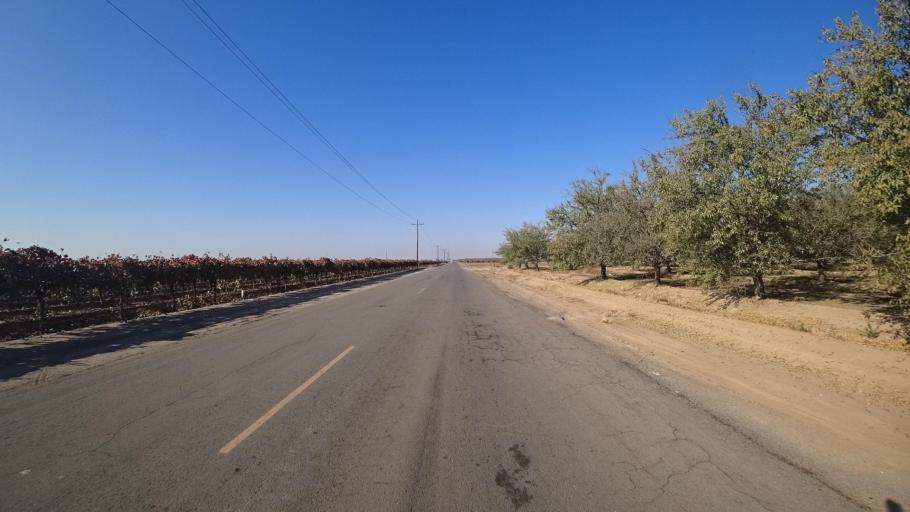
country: US
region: California
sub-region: Kern County
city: Delano
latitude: 35.7469
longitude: -119.2175
